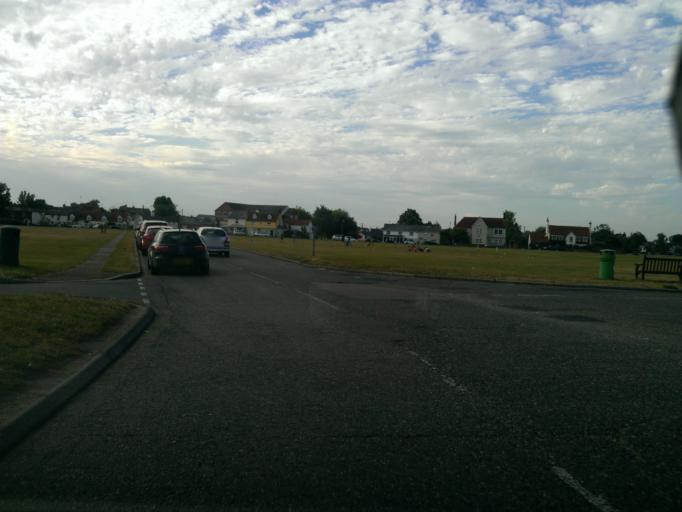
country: GB
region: England
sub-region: Essex
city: Great Bentley
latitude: 51.8531
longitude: 1.0640
